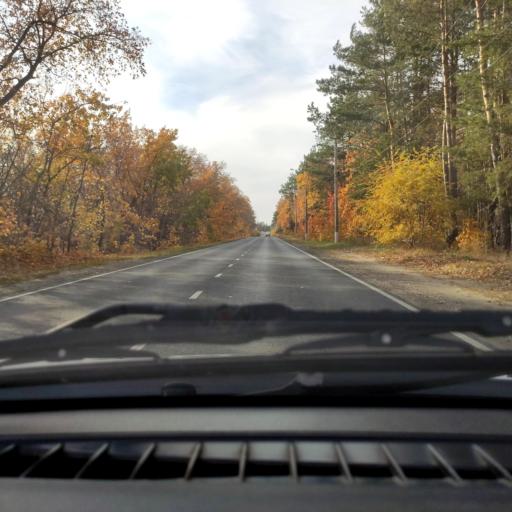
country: RU
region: Samara
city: Tol'yatti
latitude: 53.4734
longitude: 49.3981
